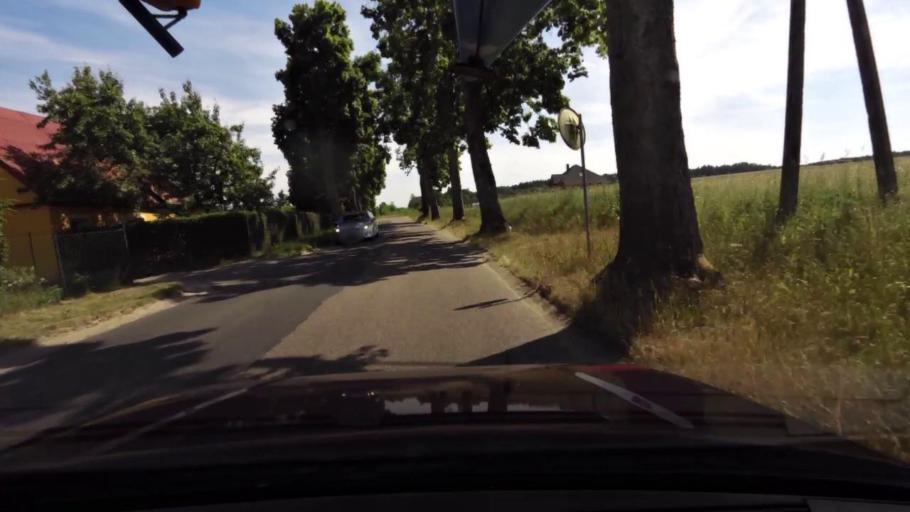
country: PL
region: Pomeranian Voivodeship
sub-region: Powiat slupski
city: Kobylnica
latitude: 54.3781
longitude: 16.9655
